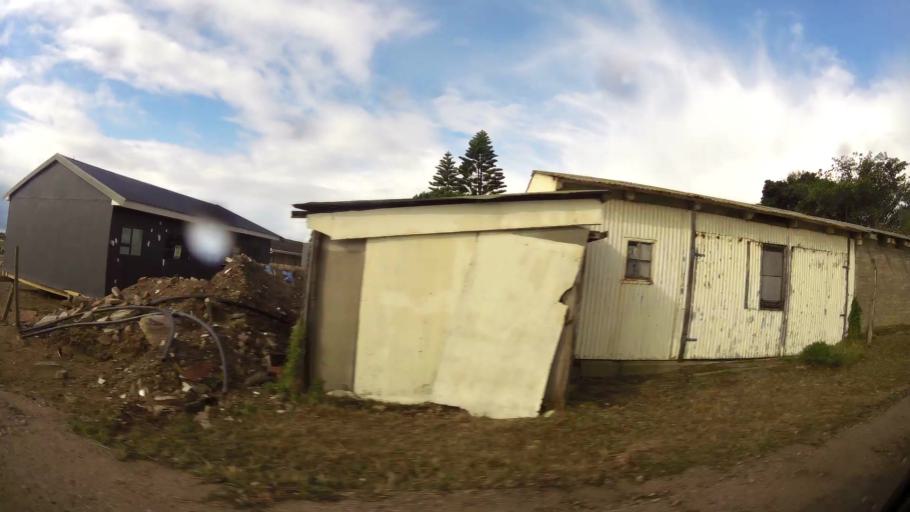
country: ZA
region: Western Cape
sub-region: Eden District Municipality
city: Mossel Bay
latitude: -34.1864
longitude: 22.1213
